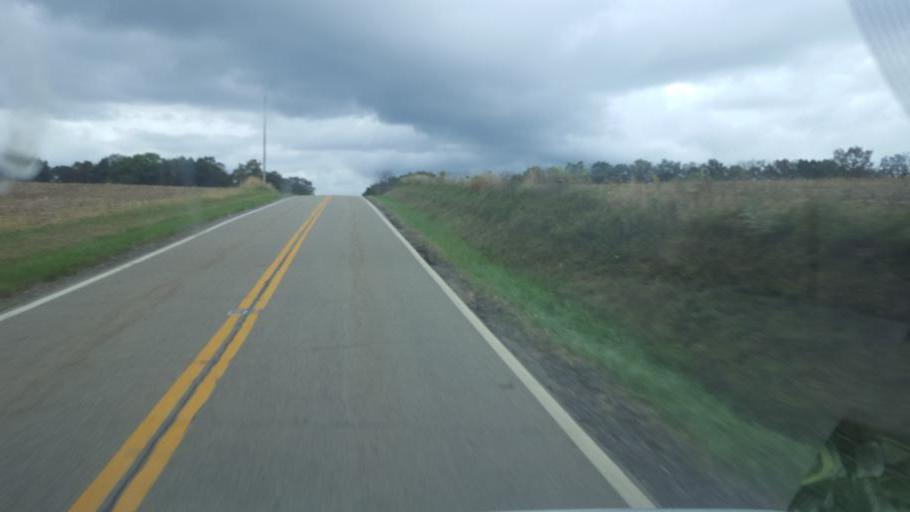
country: US
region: Ohio
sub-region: Ashland County
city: Loudonville
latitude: 40.5495
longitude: -82.1632
